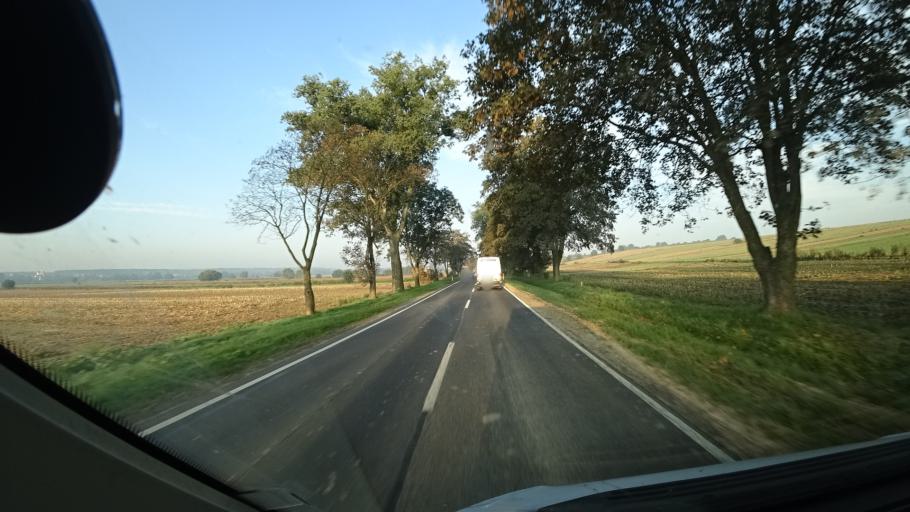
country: PL
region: Opole Voivodeship
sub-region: Powiat strzelecki
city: Ujazd
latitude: 50.3868
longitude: 18.3743
